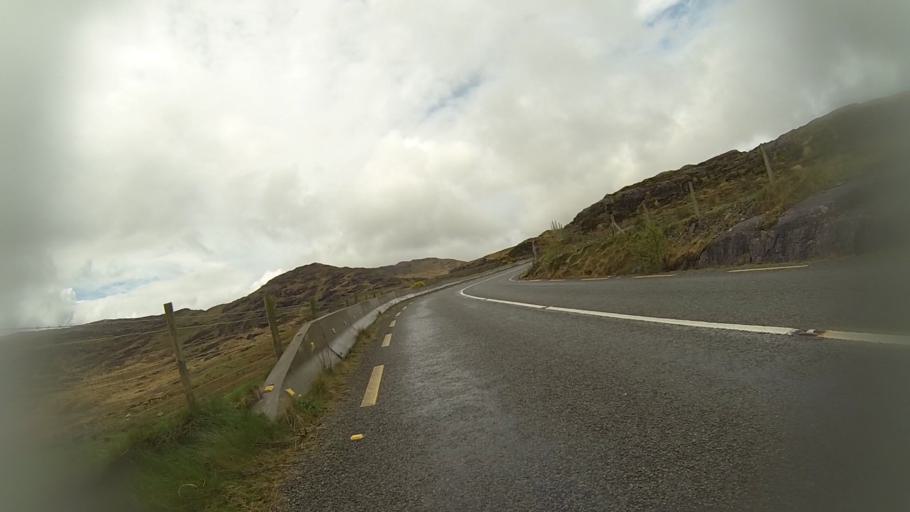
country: IE
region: Munster
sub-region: Ciarrai
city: Kenmare
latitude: 51.7963
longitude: -9.5824
